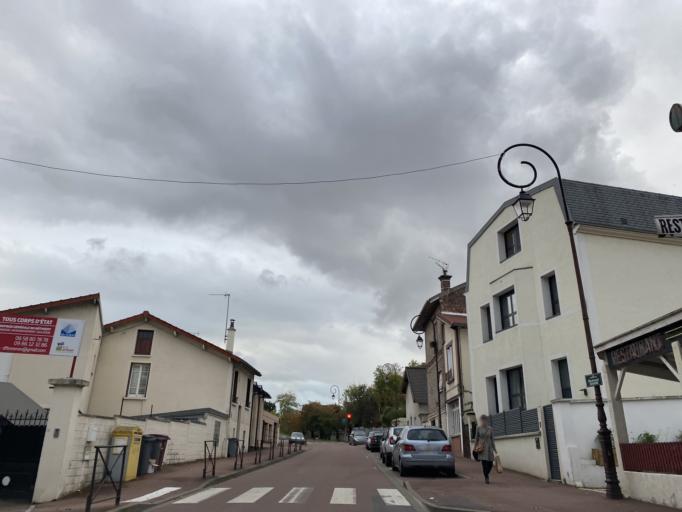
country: FR
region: Ile-de-France
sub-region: Departement des Hauts-de-Seine
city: Saint-Cloud
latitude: 48.8509
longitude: 2.2215
